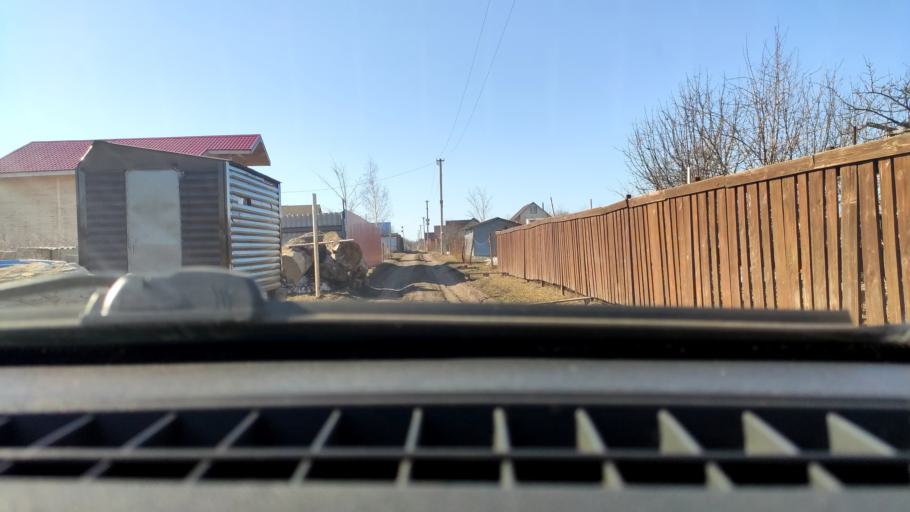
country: RU
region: Bashkortostan
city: Kabakovo
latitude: 54.7154
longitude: 56.1702
